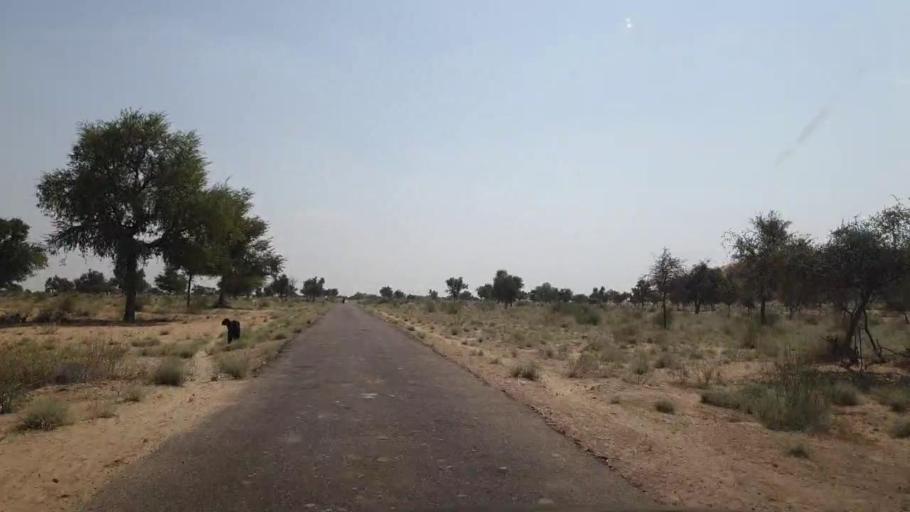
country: PK
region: Sindh
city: Islamkot
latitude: 25.1020
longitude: 70.7248
